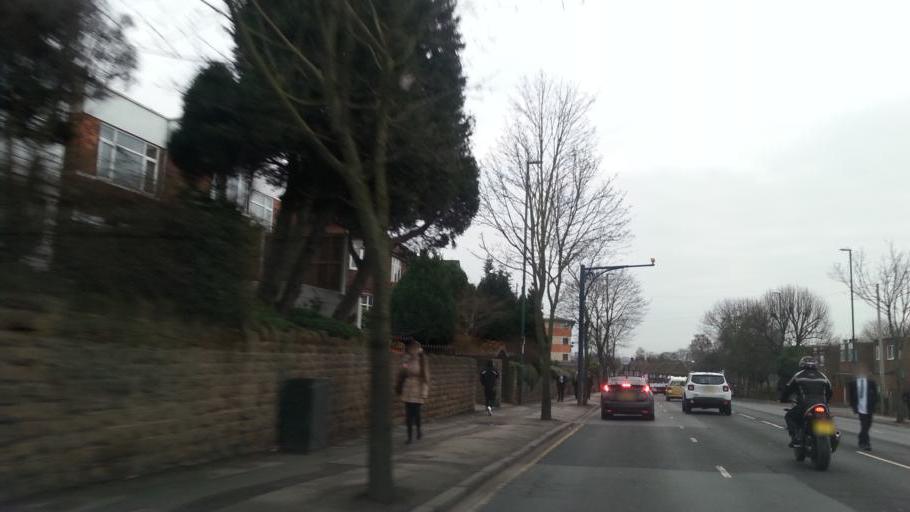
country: GB
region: England
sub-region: Nottingham
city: Nottingham
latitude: 52.9791
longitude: -1.1927
